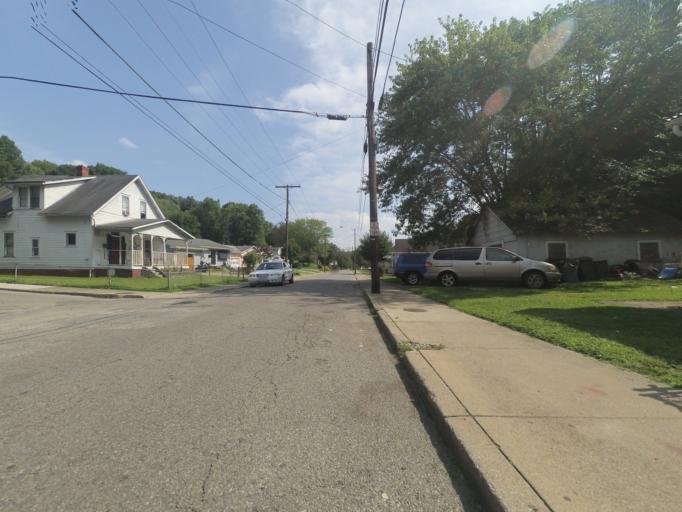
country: US
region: West Virginia
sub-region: Cabell County
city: Huntington
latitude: 38.4138
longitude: -82.4016
